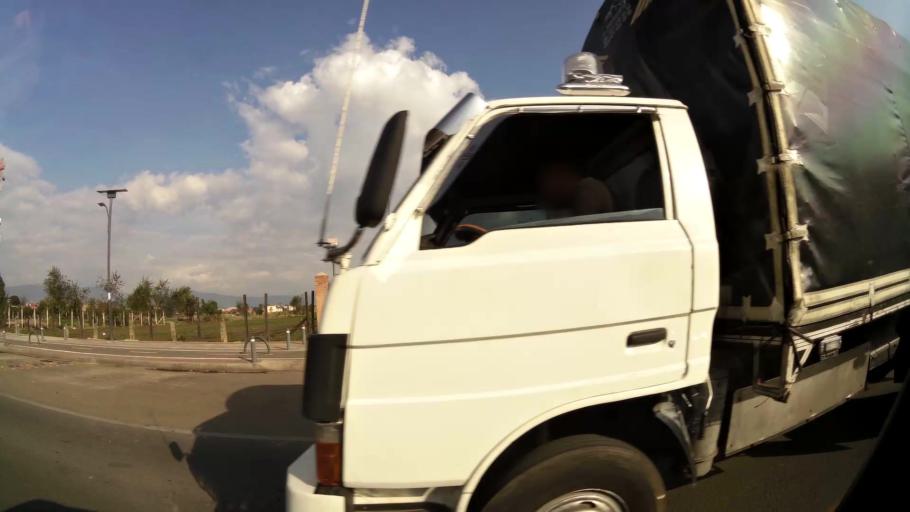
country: CO
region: Cundinamarca
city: Cota
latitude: 4.8058
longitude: -74.1053
